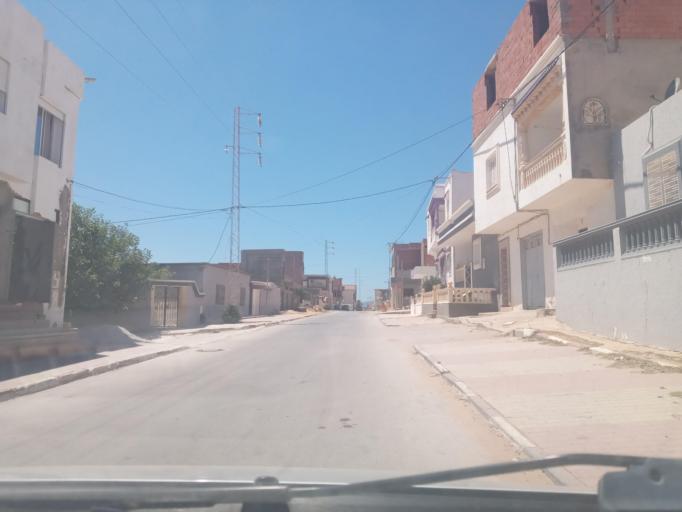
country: TN
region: Nabul
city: El Haouaria
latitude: 37.0497
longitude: 11.0034
